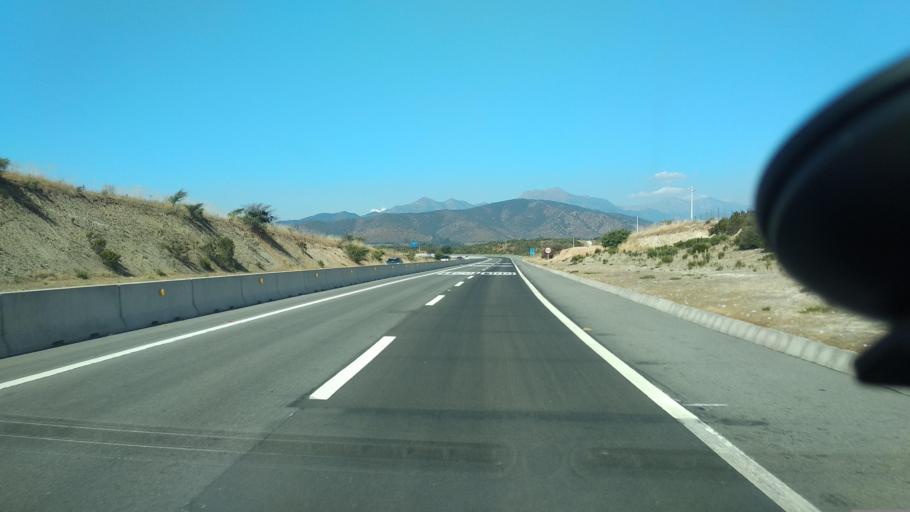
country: CL
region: Valparaiso
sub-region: Provincia de Marga Marga
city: Limache
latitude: -32.9873
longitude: -71.3239
